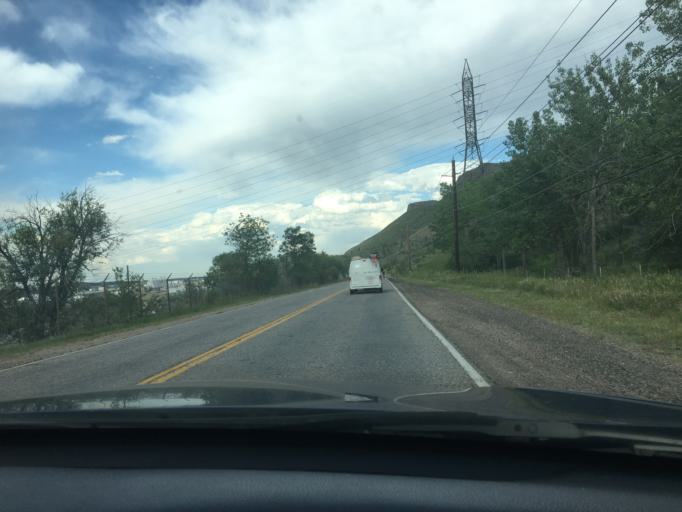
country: US
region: Colorado
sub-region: Jefferson County
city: Golden
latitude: 39.7634
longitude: -105.2059
